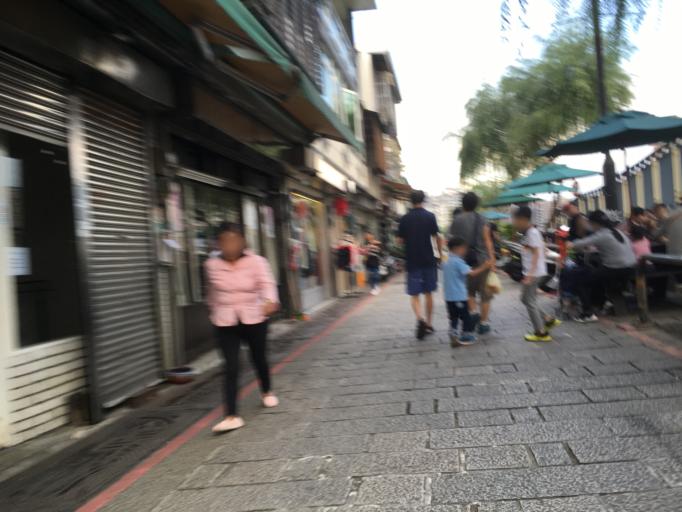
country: TW
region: Taiwan
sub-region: Taoyuan
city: Taoyuan
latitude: 24.9337
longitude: 121.3709
